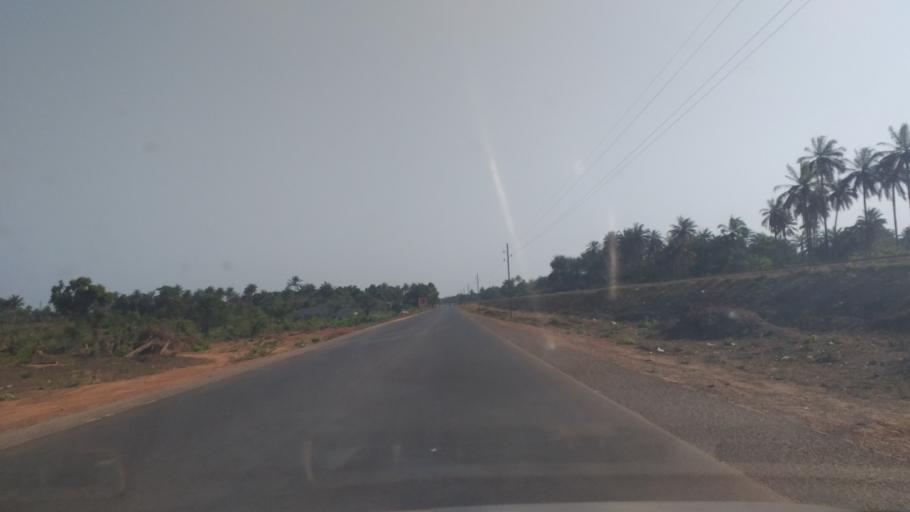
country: GN
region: Boke
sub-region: Boke Prefecture
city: Kamsar
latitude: 10.7482
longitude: -14.5092
